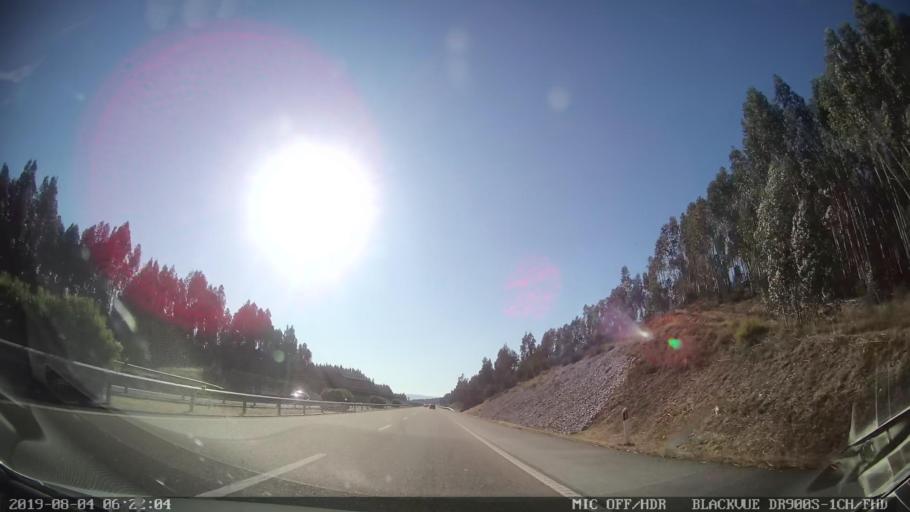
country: PT
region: Santarem
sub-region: Chamusca
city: Vila Nova da Barquinha
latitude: 39.4866
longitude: -8.4178
